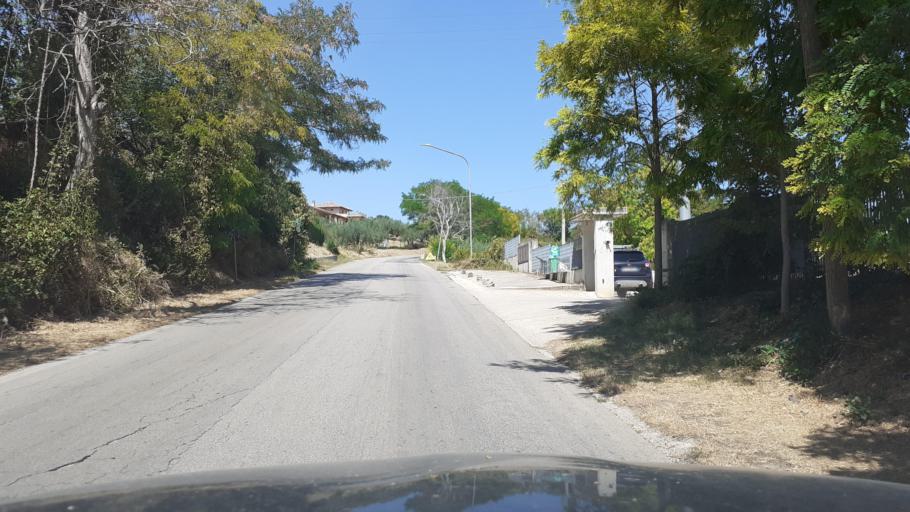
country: IT
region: Abruzzo
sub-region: Provincia di Chieti
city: Santa Maria Imbaro
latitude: 42.2165
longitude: 14.4540
